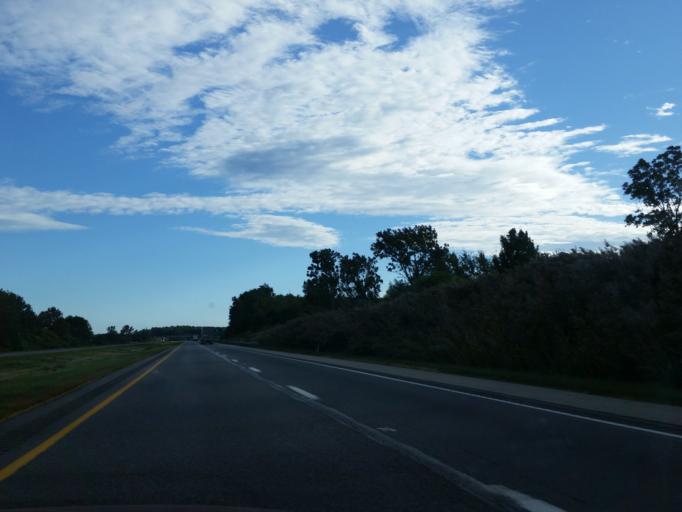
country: US
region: Pennsylvania
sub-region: Erie County
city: North East
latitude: 42.2174
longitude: -79.7934
